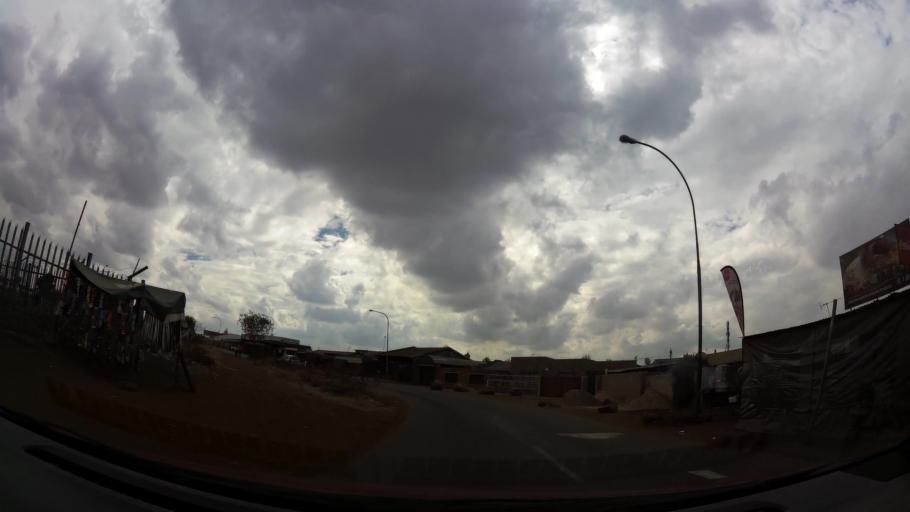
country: ZA
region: Gauteng
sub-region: City of Johannesburg Metropolitan Municipality
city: Soweto
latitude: -26.2539
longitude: 27.8329
